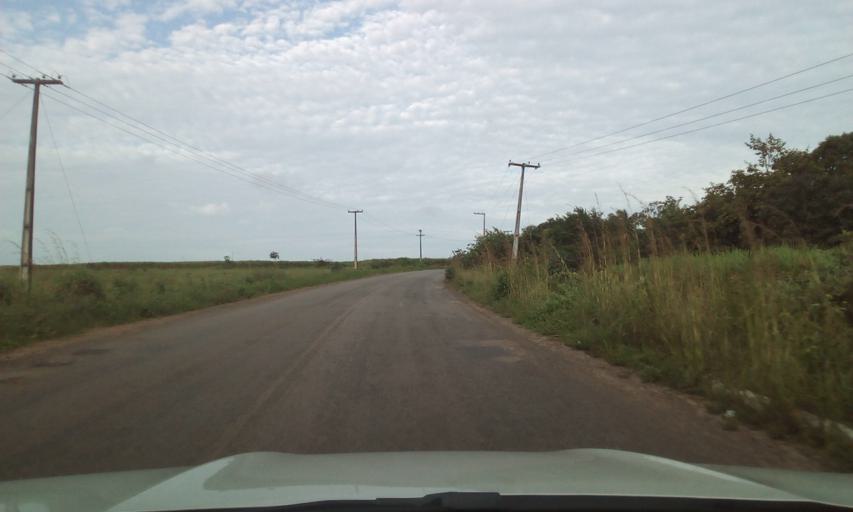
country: BR
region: Paraiba
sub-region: Conde
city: Conde
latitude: -7.2689
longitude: -34.8783
